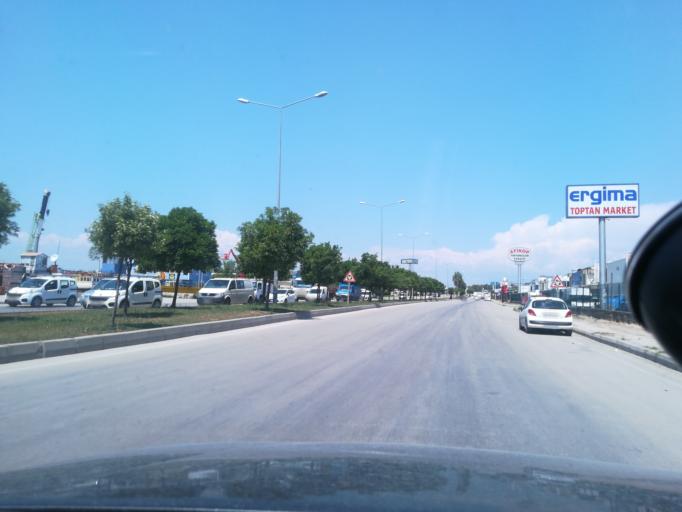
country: TR
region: Adana
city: Seyhan
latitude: 36.9914
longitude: 35.2527
